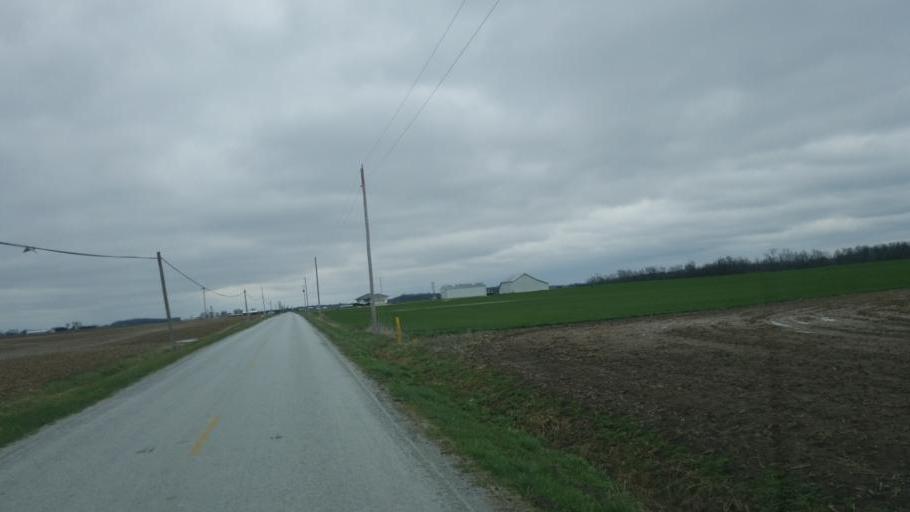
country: US
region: Ohio
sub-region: Hardin County
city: Kenton
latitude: 40.6584
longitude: -83.5352
